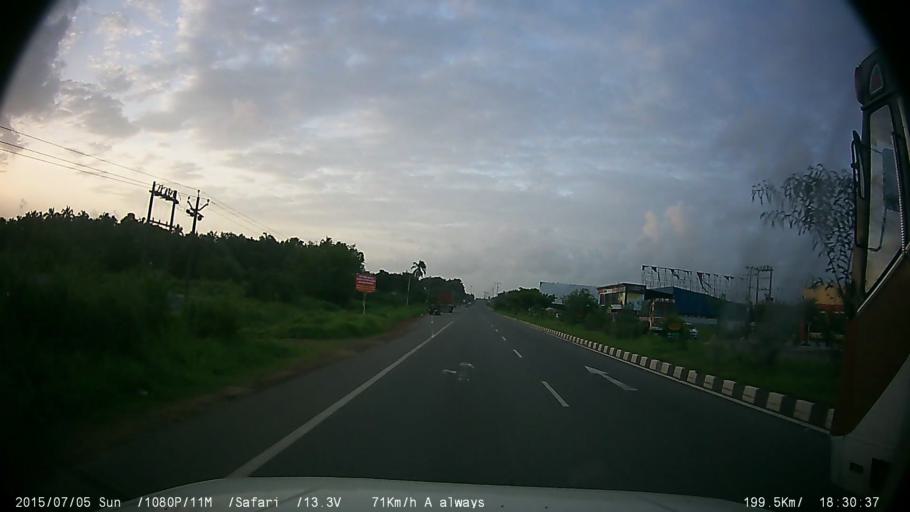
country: IN
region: Kerala
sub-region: Thrissur District
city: Trichur
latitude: 10.4846
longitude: 76.2577
